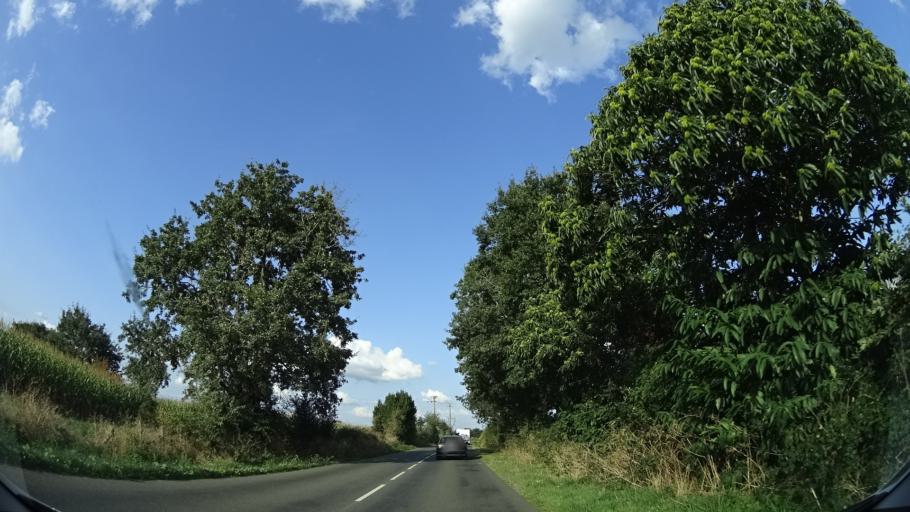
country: FR
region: Pays de la Loire
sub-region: Departement de la Loire-Atlantique
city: Nort-sur-Erdre
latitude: 47.4155
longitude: -1.5278
